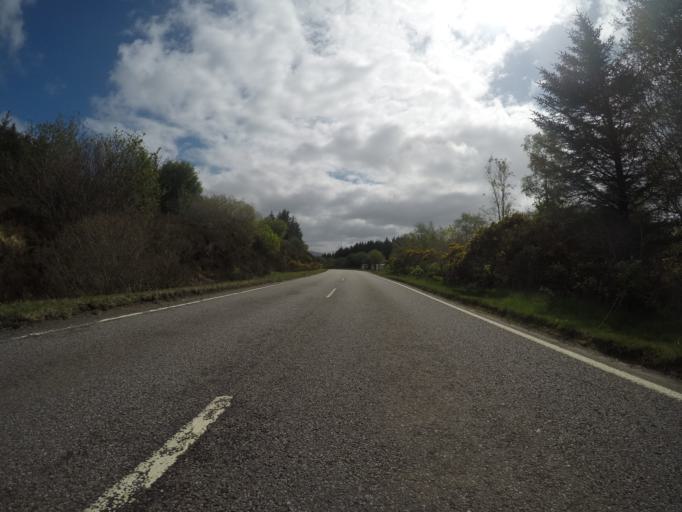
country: GB
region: Scotland
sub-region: Highland
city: Portree
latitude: 57.2462
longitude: -5.9272
